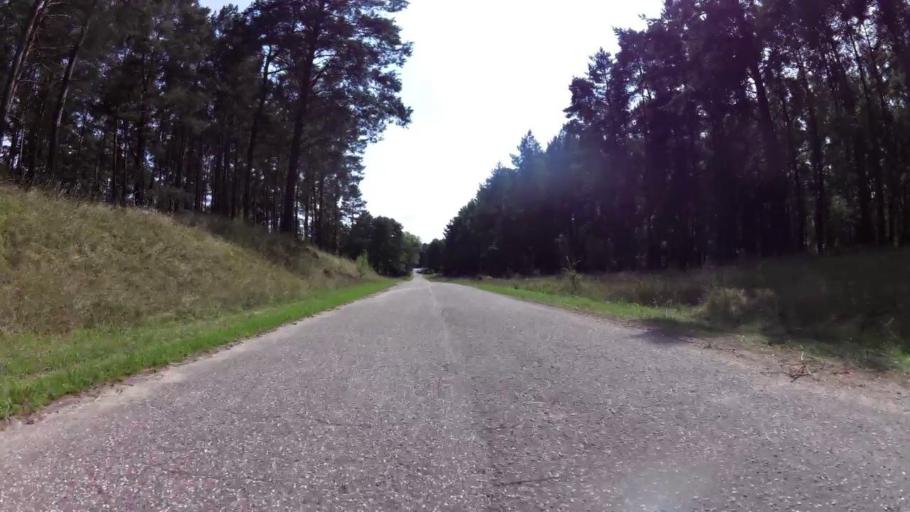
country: PL
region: West Pomeranian Voivodeship
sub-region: Powiat choszczenski
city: Drawno
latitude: 53.3202
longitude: 15.6877
